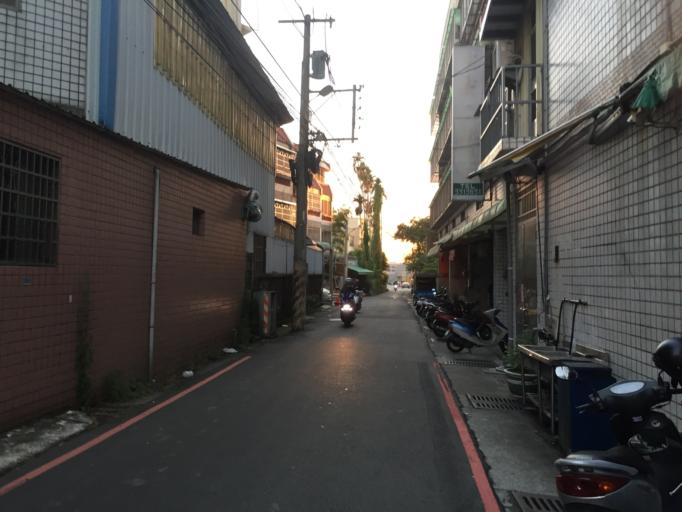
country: TW
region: Taiwan
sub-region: Taichung City
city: Taichung
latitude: 24.0733
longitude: 120.7151
